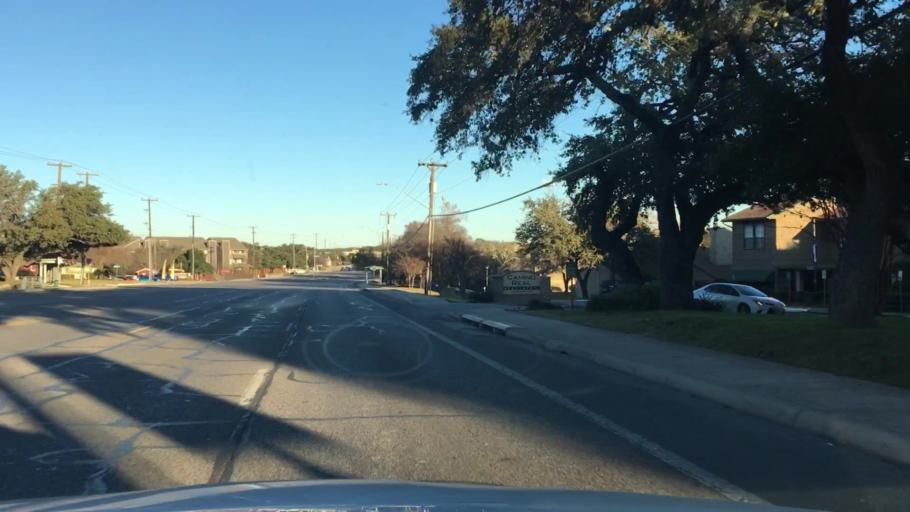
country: US
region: Texas
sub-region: Bexar County
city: Castle Hills
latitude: 29.5528
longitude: -98.5134
